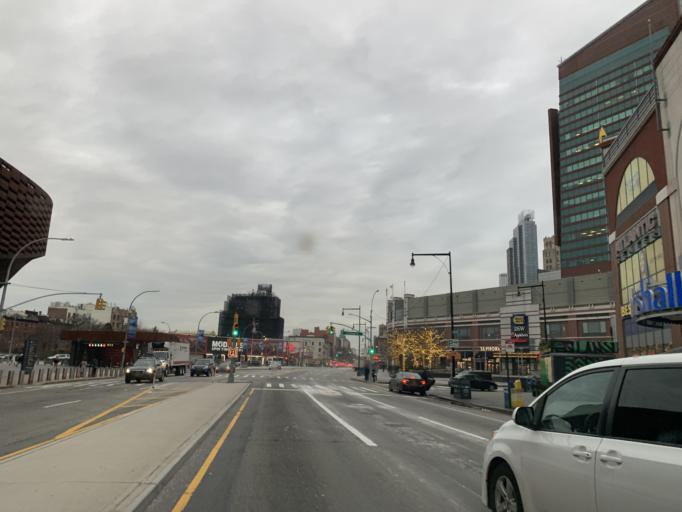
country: US
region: New York
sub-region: Kings County
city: Brooklyn
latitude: 40.6836
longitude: -73.9753
